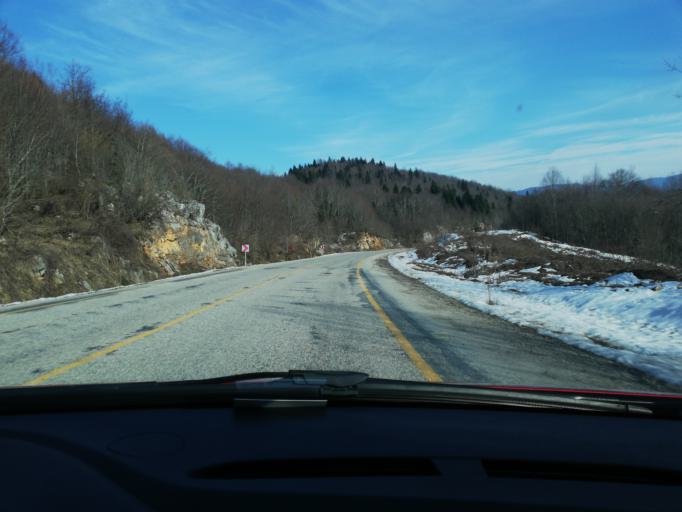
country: TR
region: Kastamonu
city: Cide
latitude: 41.8157
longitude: 33.1010
